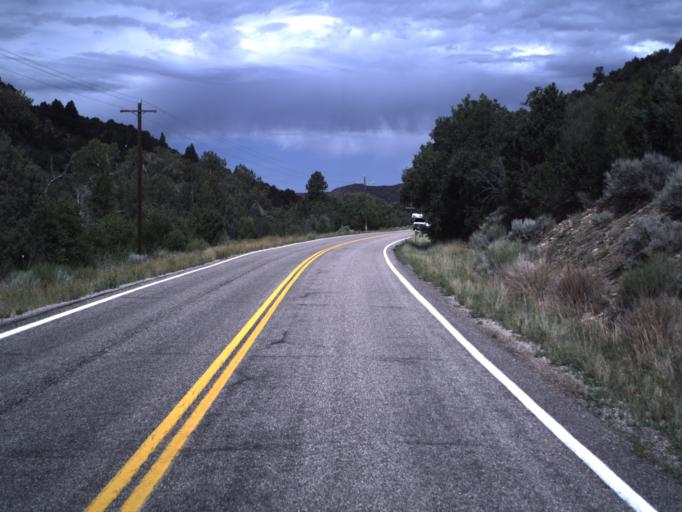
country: US
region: Utah
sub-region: Iron County
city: Cedar City
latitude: 37.6443
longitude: -112.9656
